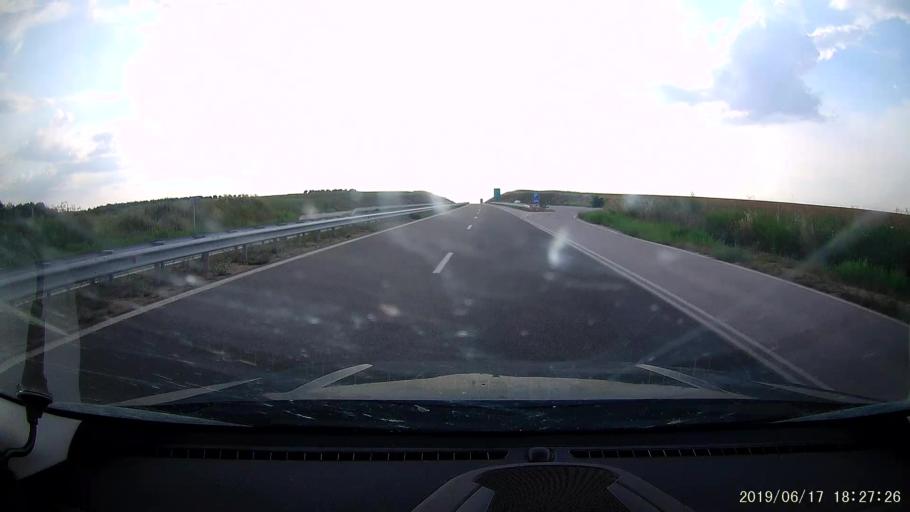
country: BG
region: Khaskovo
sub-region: Obshtina Dimitrovgrad
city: Dimitrovgrad
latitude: 42.0169
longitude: 25.6087
